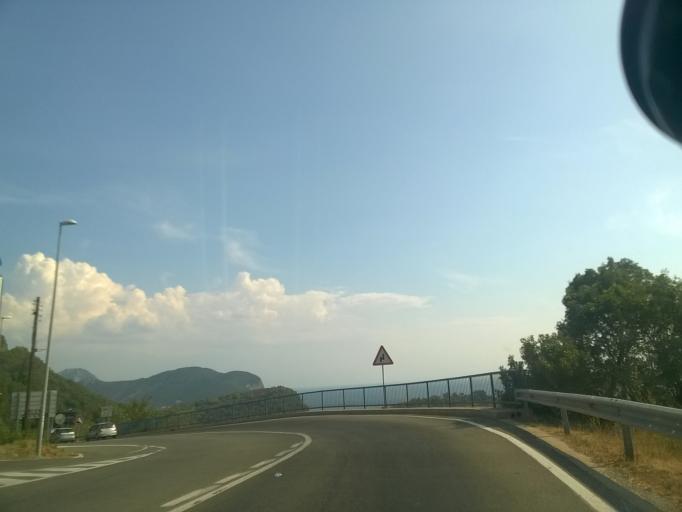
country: ME
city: Petrovac na Moru
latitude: 42.2108
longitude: 18.9447
